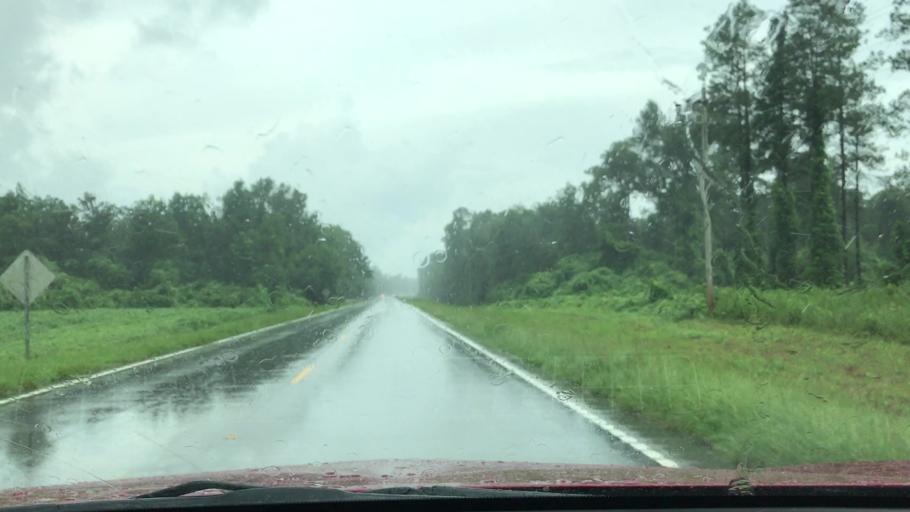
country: US
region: South Carolina
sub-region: Horry County
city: Socastee
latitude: 33.6828
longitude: -79.1251
